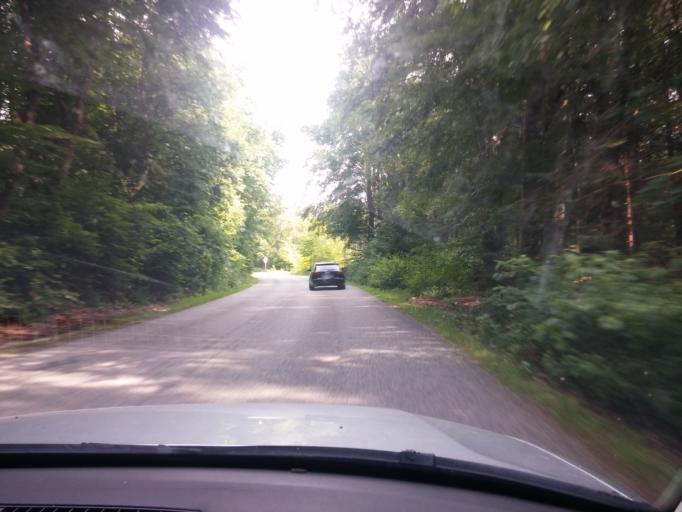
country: DE
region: Bavaria
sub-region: Upper Bavaria
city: Kirchseeon
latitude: 48.0633
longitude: 11.8932
